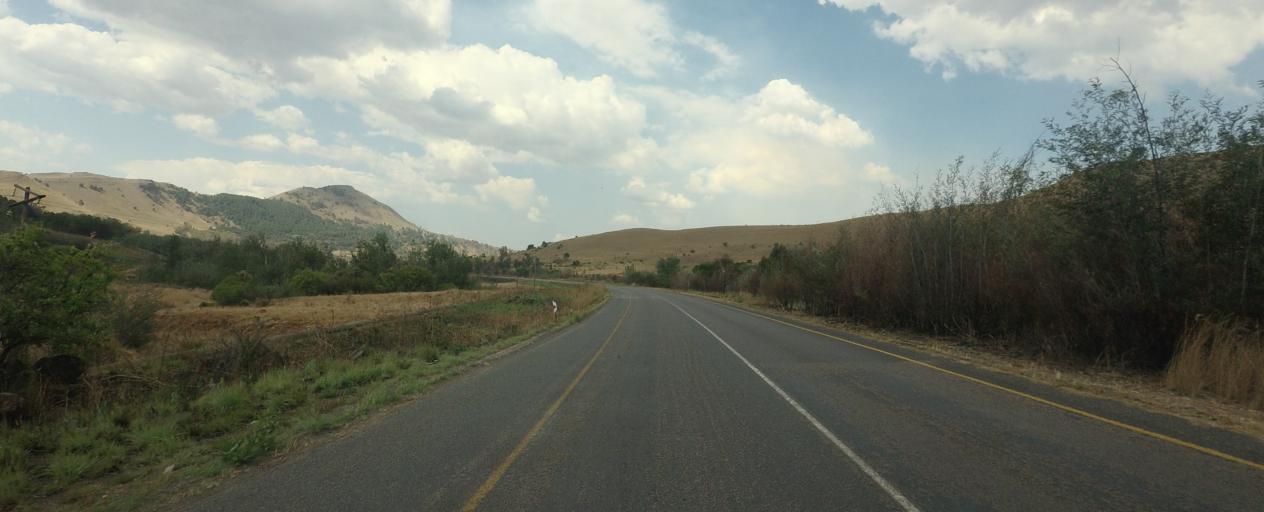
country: ZA
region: Mpumalanga
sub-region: Ehlanzeni District
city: Lydenburg
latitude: -25.2262
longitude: 30.3111
